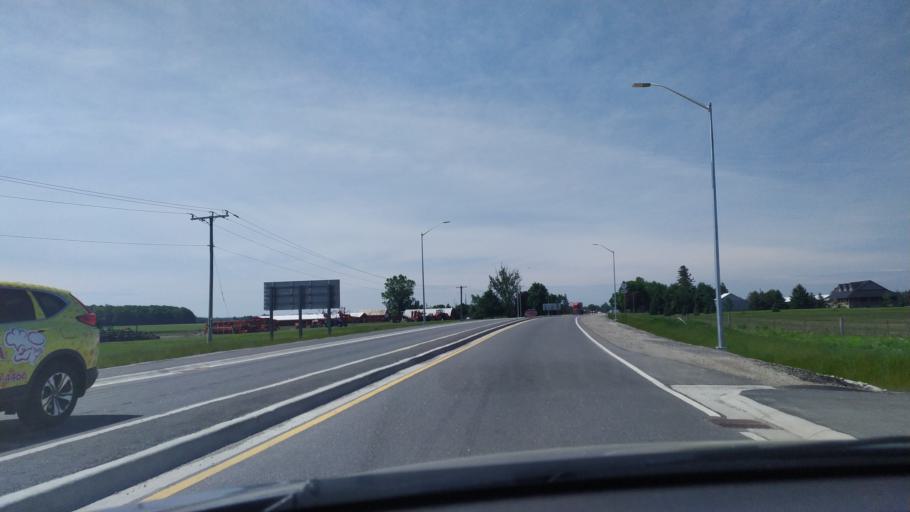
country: CA
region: Ontario
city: Stratford
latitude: 43.3240
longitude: -81.0229
